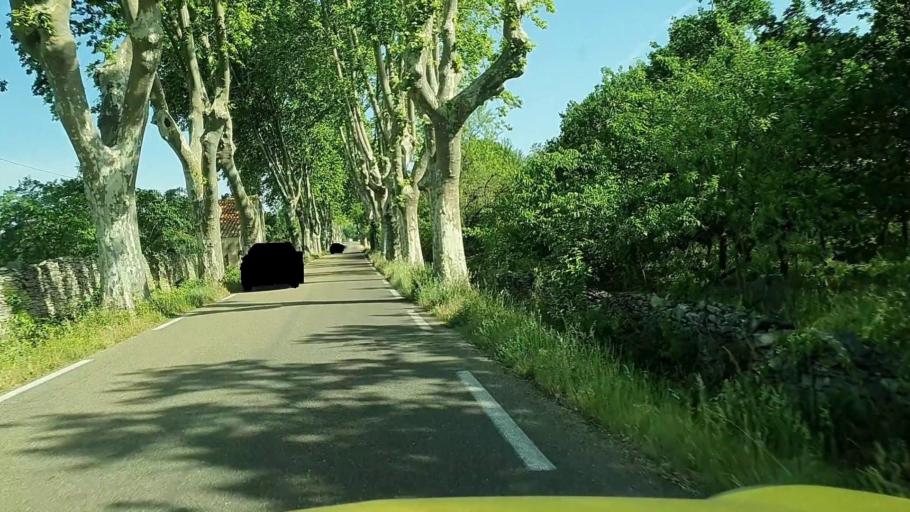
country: FR
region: Languedoc-Roussillon
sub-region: Departement du Gard
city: Montaren-et-Saint-Mediers
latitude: 44.0423
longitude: 4.4065
